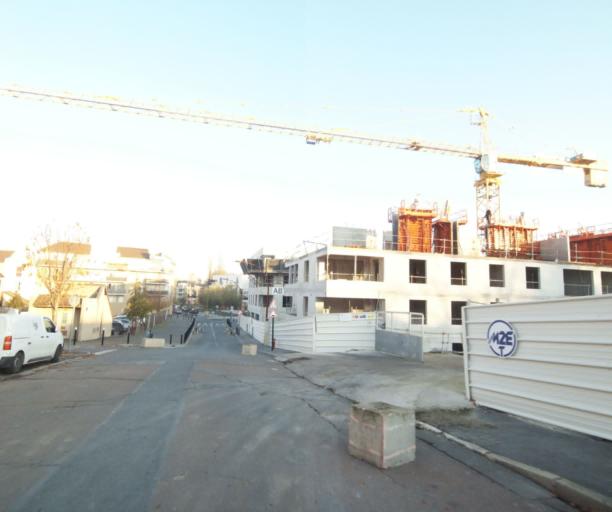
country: FR
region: Ile-de-France
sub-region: Departement du Val-d'Oise
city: Gonesse
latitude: 48.9837
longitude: 2.4523
